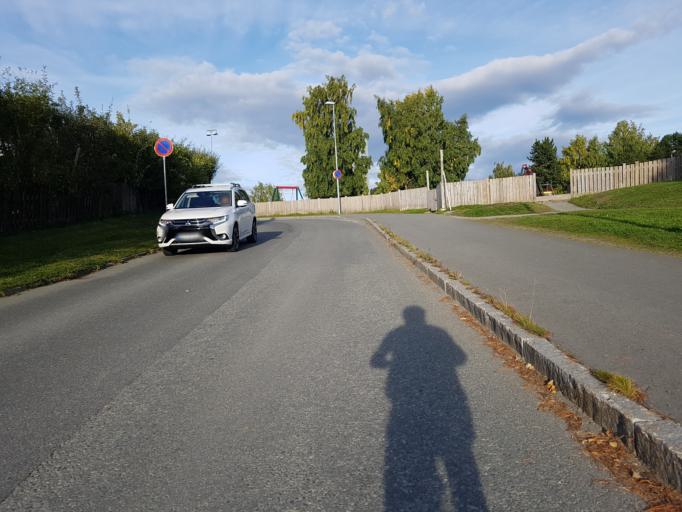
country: NO
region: Sor-Trondelag
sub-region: Trondheim
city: Trondheim
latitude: 63.3895
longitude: 10.4262
